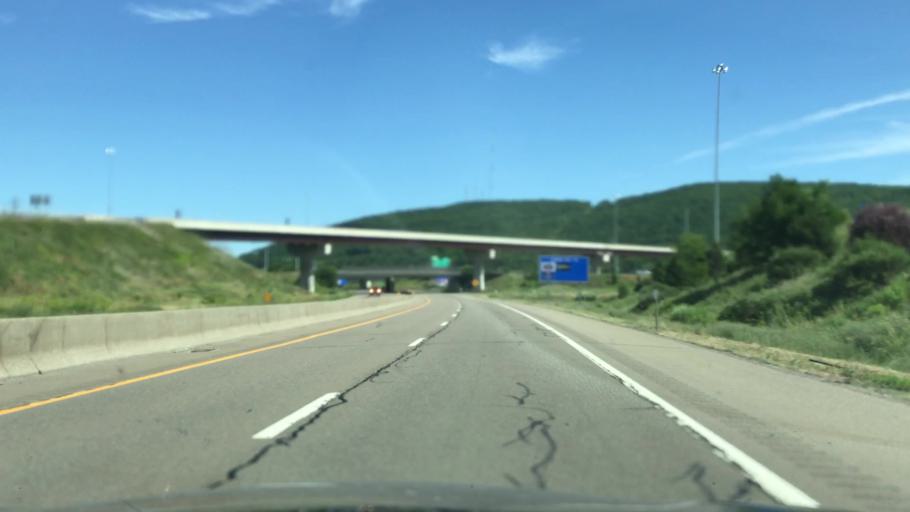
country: US
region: New York
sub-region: Steuben County
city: Painted Post
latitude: 42.1580
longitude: -77.0986
